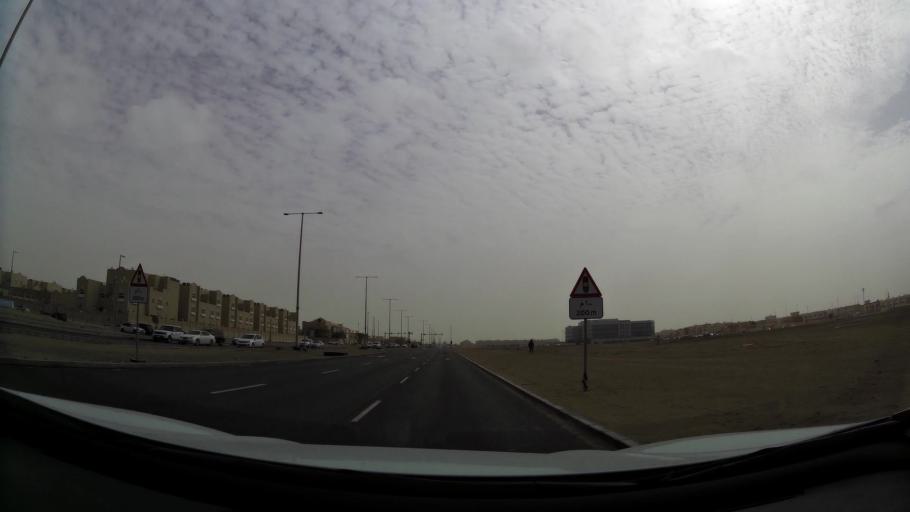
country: AE
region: Abu Dhabi
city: Abu Dhabi
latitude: 24.4104
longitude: 54.5696
